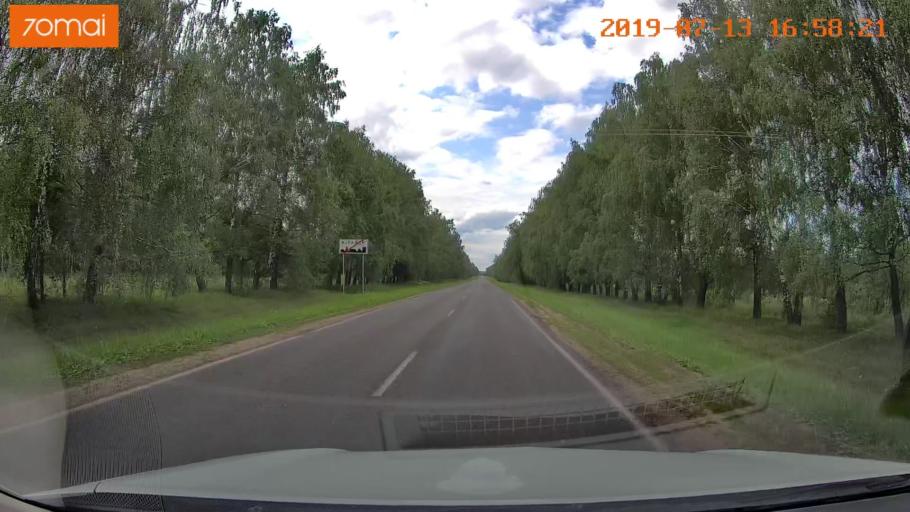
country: BY
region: Mogilev
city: Kirawsk
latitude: 53.2874
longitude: 29.4429
